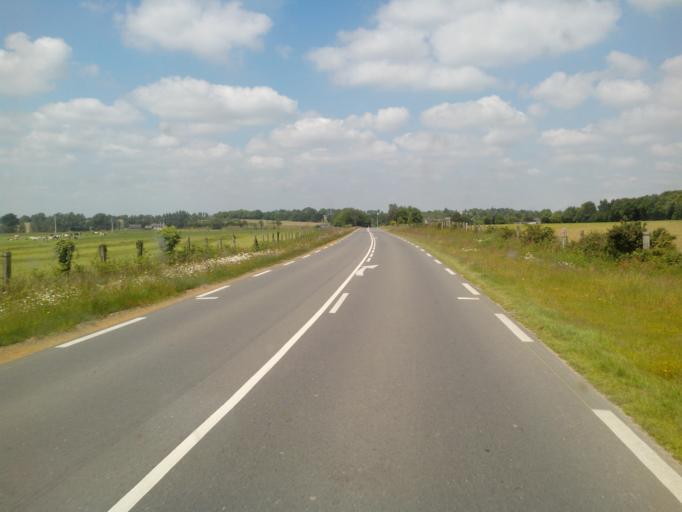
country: FR
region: Brittany
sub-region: Departement d'Ille-et-Vilaine
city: Saint-Germain-en-Cogles
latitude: 48.3926
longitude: -1.2860
